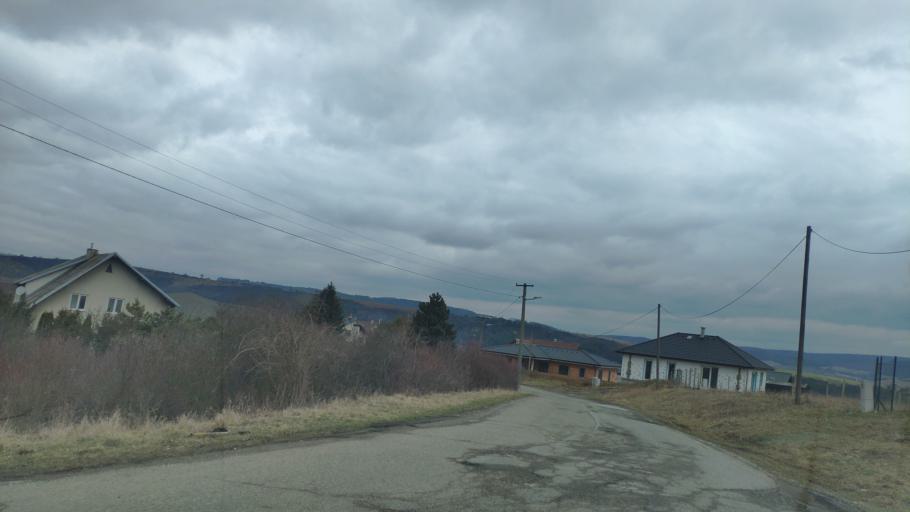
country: SK
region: Presovsky
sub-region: Okres Presov
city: Presov
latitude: 49.0828
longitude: 21.2710
